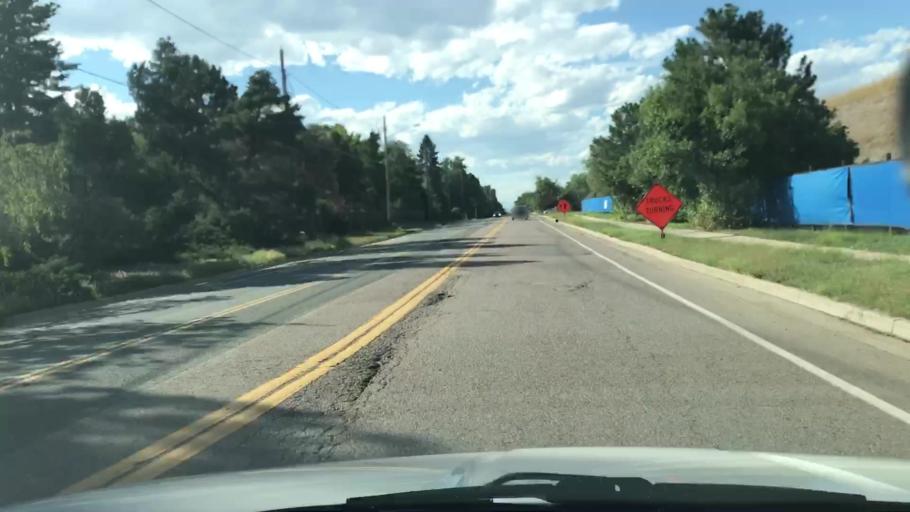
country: US
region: Colorado
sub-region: Arapahoe County
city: Greenwood Village
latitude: 39.6396
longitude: -104.9144
